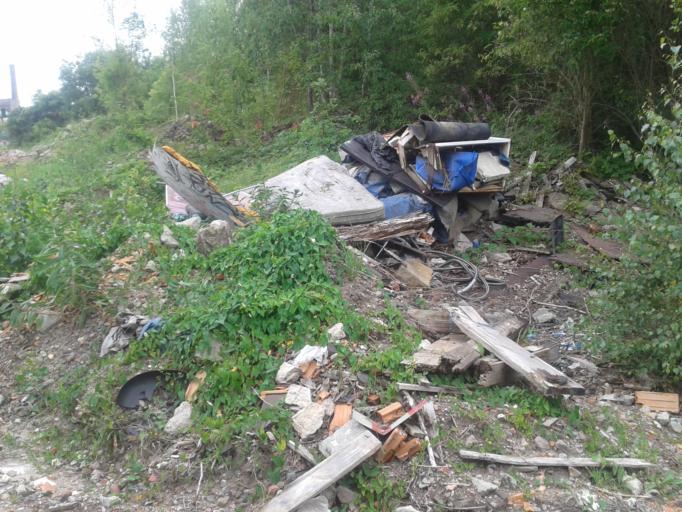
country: DE
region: Saxony
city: Dresden
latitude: 51.0696
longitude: 13.7357
